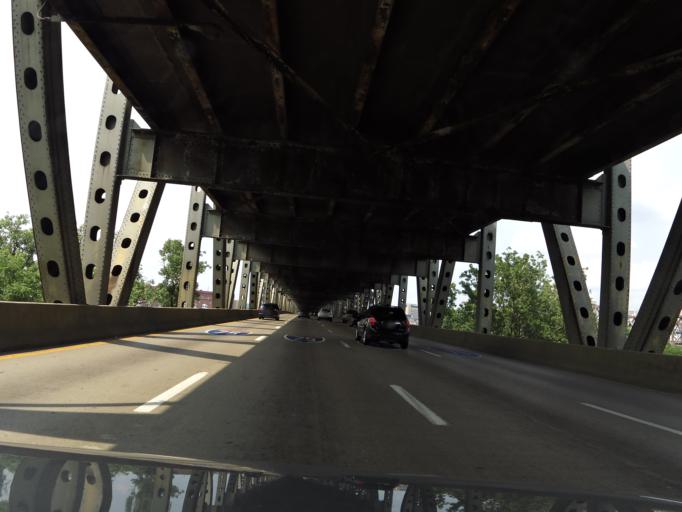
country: US
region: Kentucky
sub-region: Kenton County
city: Covington
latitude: 39.0887
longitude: -84.5227
